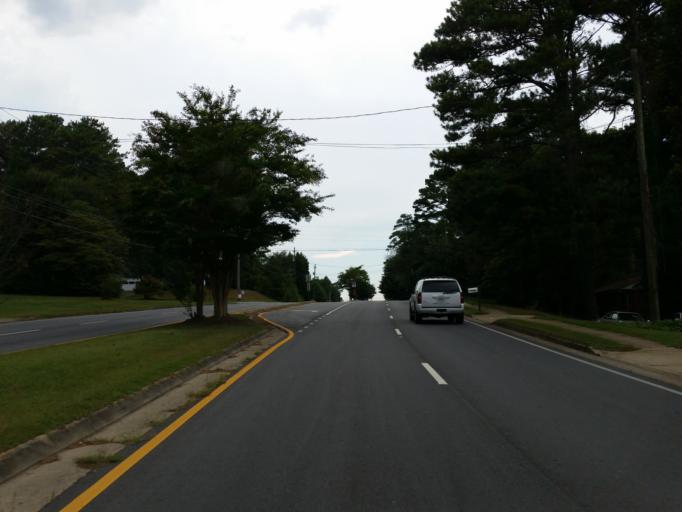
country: US
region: Georgia
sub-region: Cobb County
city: Marietta
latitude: 34.0138
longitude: -84.5421
